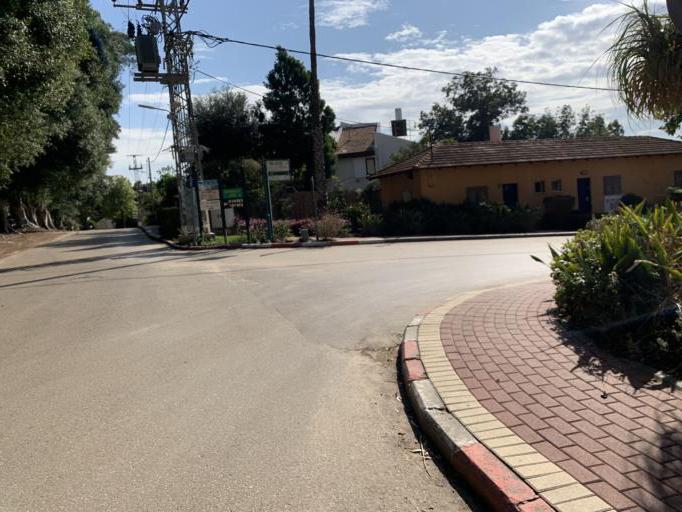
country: IL
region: Central District
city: Ra'anana
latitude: 32.1677
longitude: 34.8753
